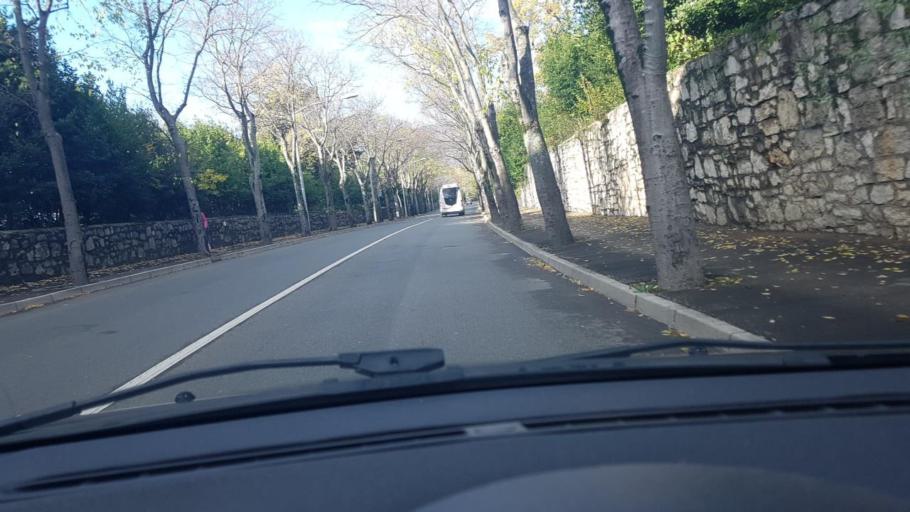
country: HR
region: Primorsko-Goranska
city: Rubesi
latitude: 45.3421
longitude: 14.3679
